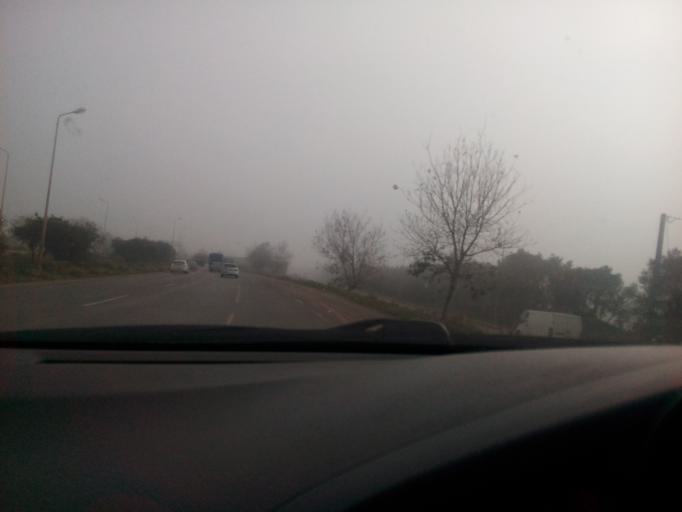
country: DZ
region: Oran
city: Es Senia
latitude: 35.6535
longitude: -0.6354
